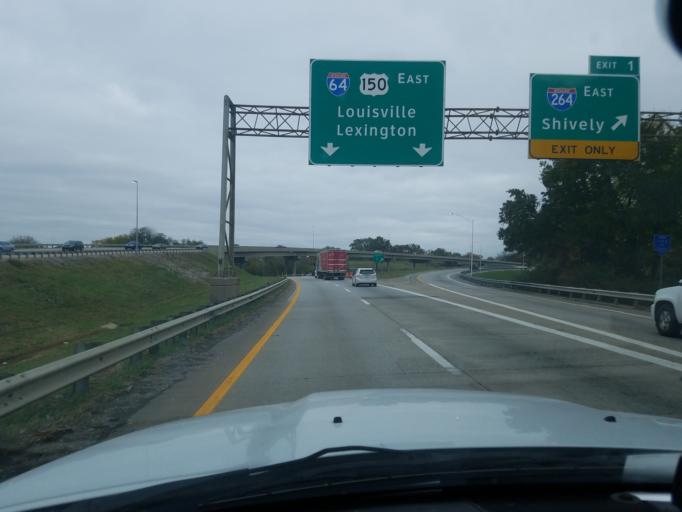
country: US
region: Indiana
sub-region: Floyd County
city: New Albany
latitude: 38.2751
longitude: -85.8126
